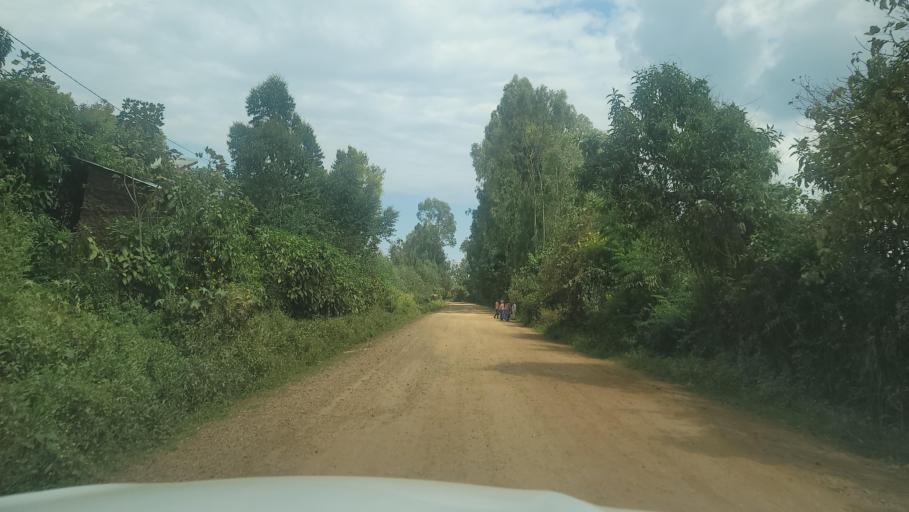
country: ET
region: Oromiya
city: Agaro
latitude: 7.7517
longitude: 36.2661
